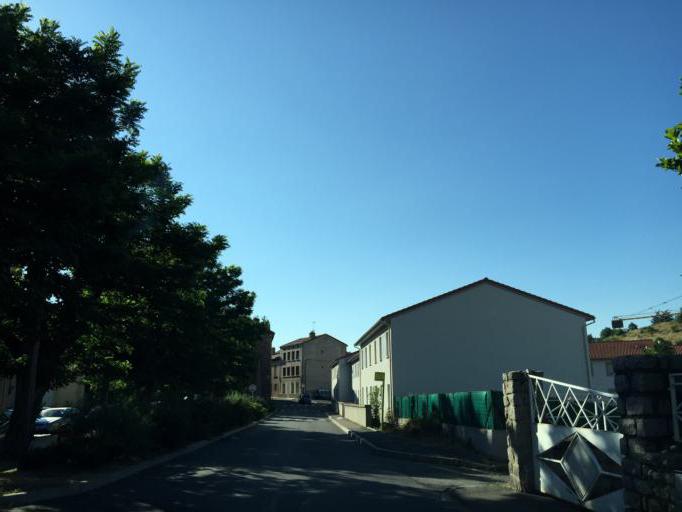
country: FR
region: Rhone-Alpes
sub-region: Departement de la Loire
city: Saint-Jean-Bonnefonds
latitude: 45.4333
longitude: 4.4418
